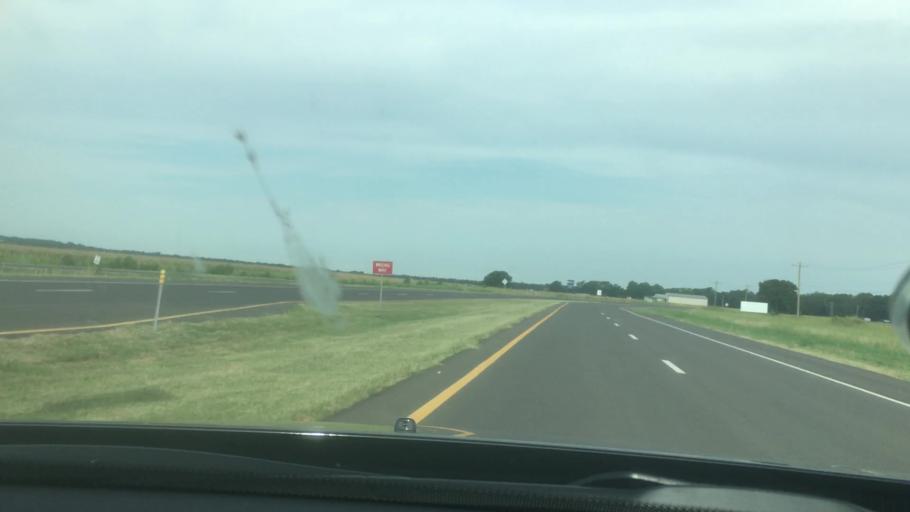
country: US
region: Oklahoma
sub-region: Garvin County
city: Pauls Valley
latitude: 34.7395
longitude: -97.2715
